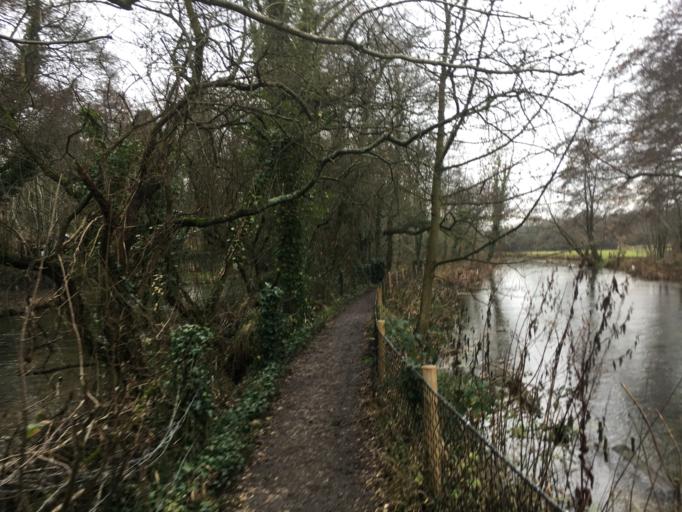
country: GB
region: England
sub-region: Hampshire
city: Compton
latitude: 50.9971
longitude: -1.3362
